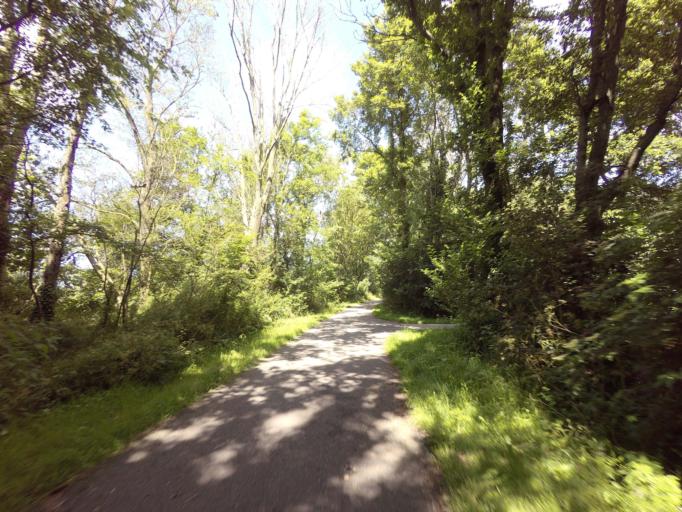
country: NL
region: North Holland
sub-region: Gemeente Den Helder
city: Den Helder
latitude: 52.9342
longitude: 4.7640
